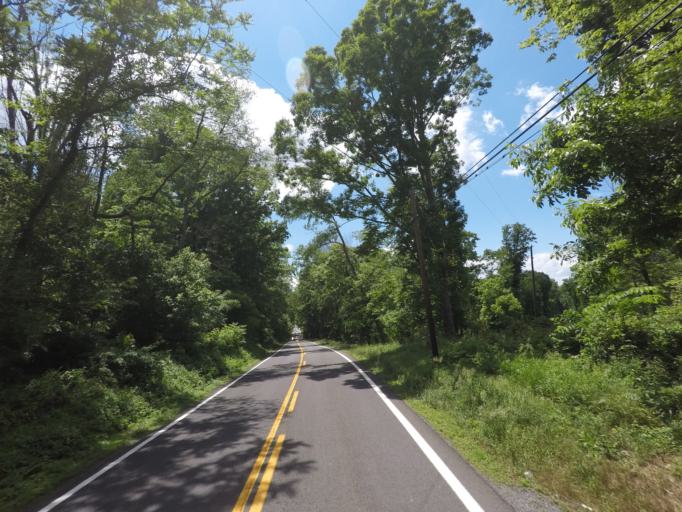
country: US
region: West Virginia
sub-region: Jefferson County
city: Shepherdstown
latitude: 39.4097
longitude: -77.8517
